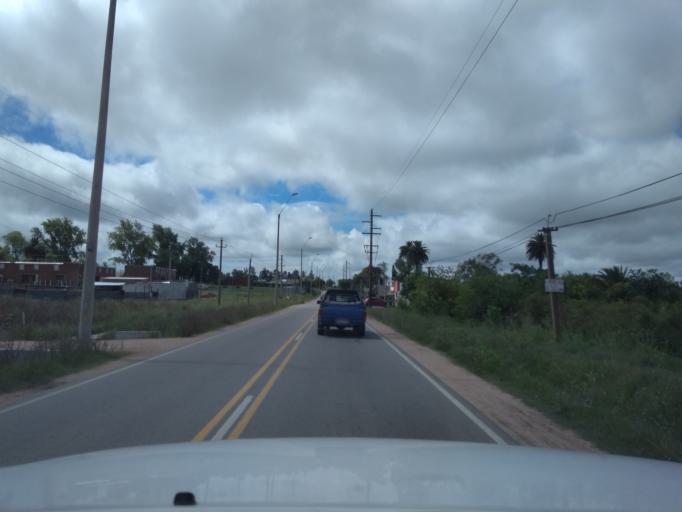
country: UY
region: Canelones
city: Pando
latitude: -34.7084
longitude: -55.9647
